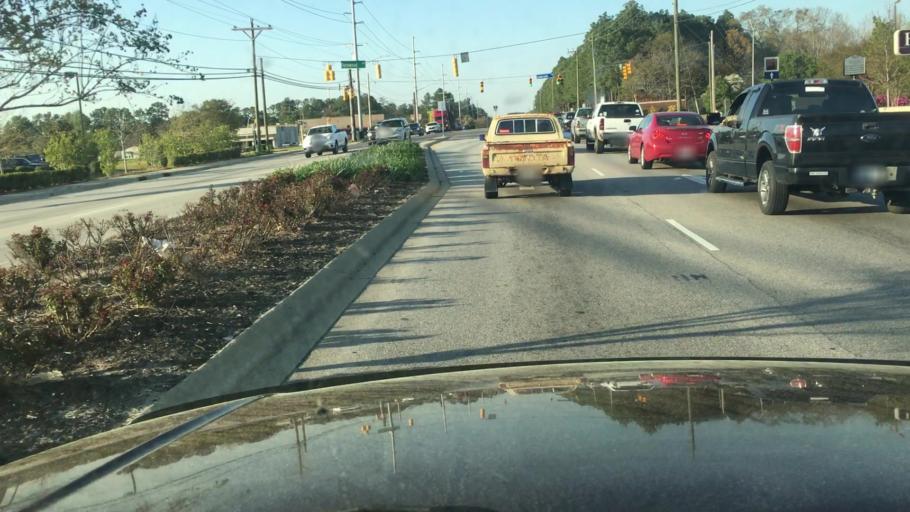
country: US
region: North Carolina
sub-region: Cumberland County
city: Fayetteville
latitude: 35.1312
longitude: -78.8779
